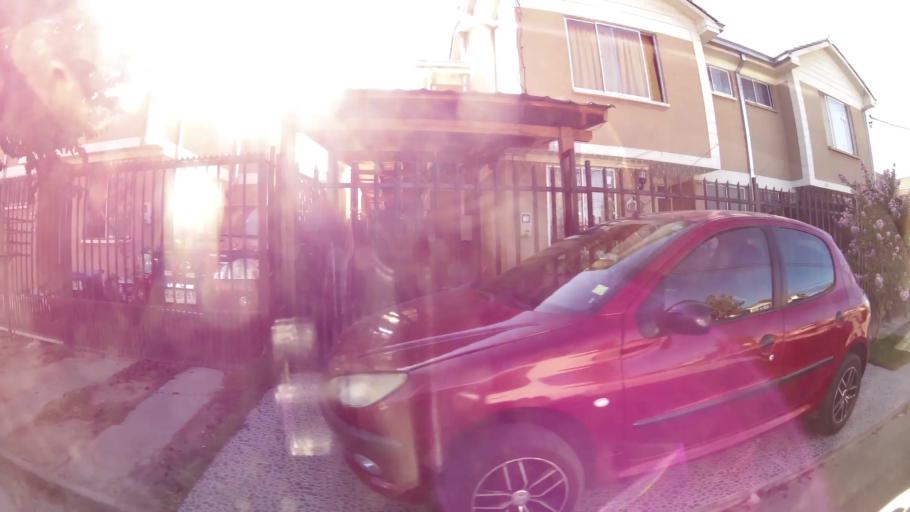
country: CL
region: O'Higgins
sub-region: Provincia de Cachapoal
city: Rancagua
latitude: -34.1793
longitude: -70.7589
